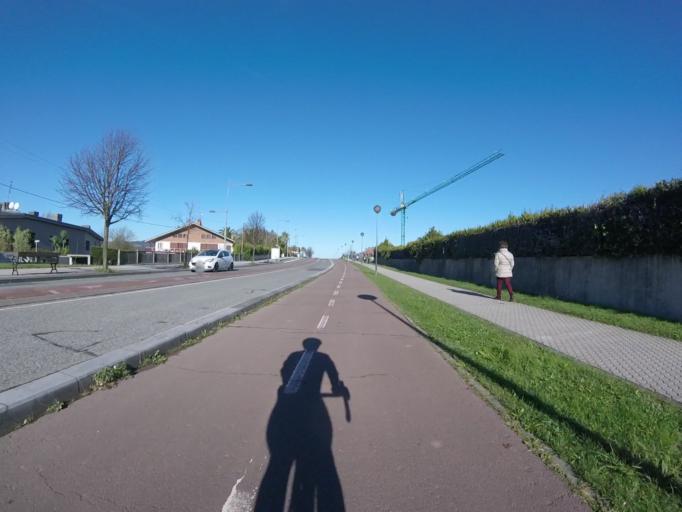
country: ES
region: Basque Country
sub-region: Provincia de Guipuzcoa
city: San Sebastian
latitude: 43.2927
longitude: -1.9911
